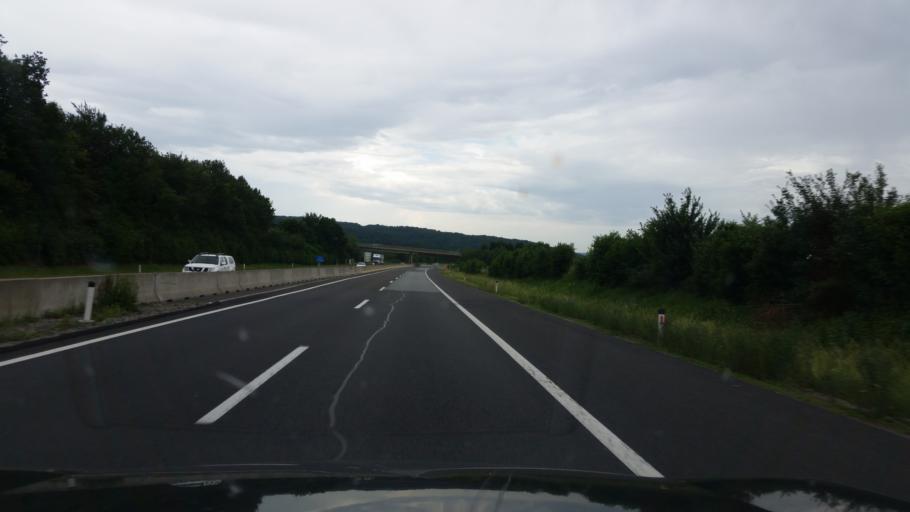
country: AT
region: Styria
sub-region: Politischer Bezirk Hartberg-Fuerstenfeld
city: Sankt Johann in der Haide
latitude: 47.2604
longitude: 16.0011
